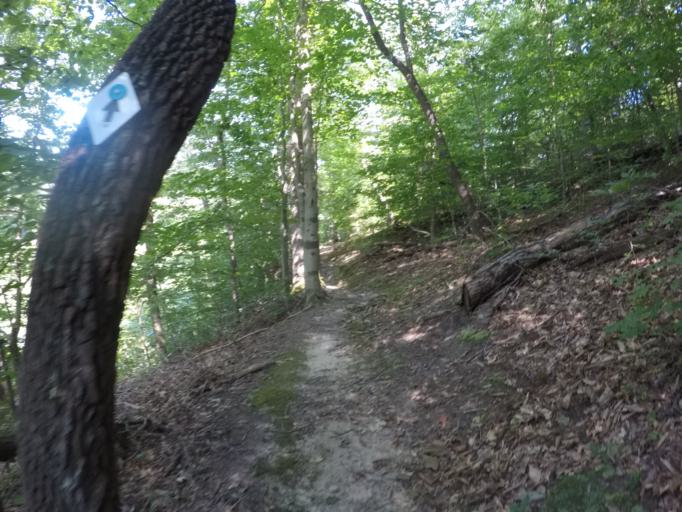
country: US
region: Ohio
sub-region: Lawrence County
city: Ironton
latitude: 38.6227
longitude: -82.6174
